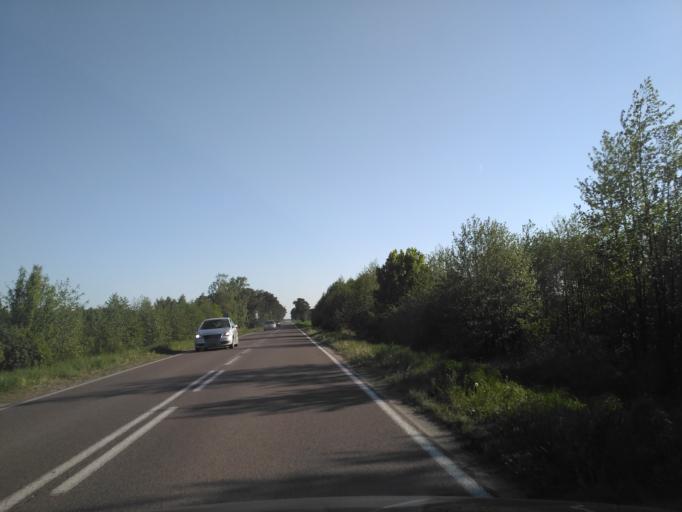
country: PL
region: Lublin Voivodeship
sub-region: Powiat swidnicki
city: Trawniki
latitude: 51.1908
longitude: 23.0555
